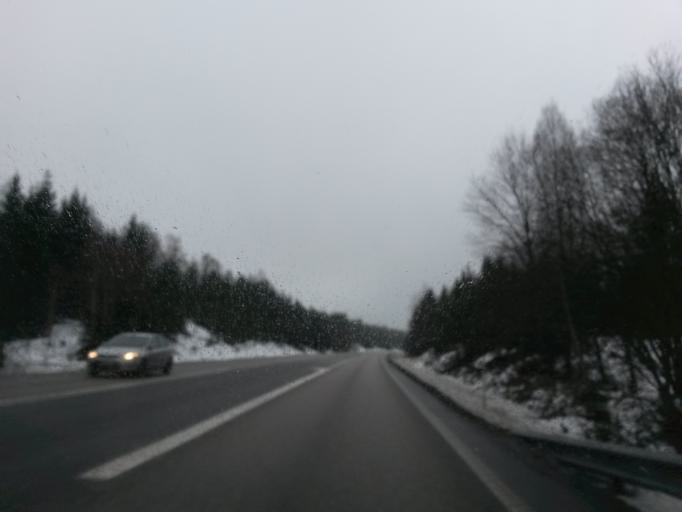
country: SE
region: Vaestra Goetaland
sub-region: Marks Kommun
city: Fritsla
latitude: 57.5226
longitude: 12.7760
